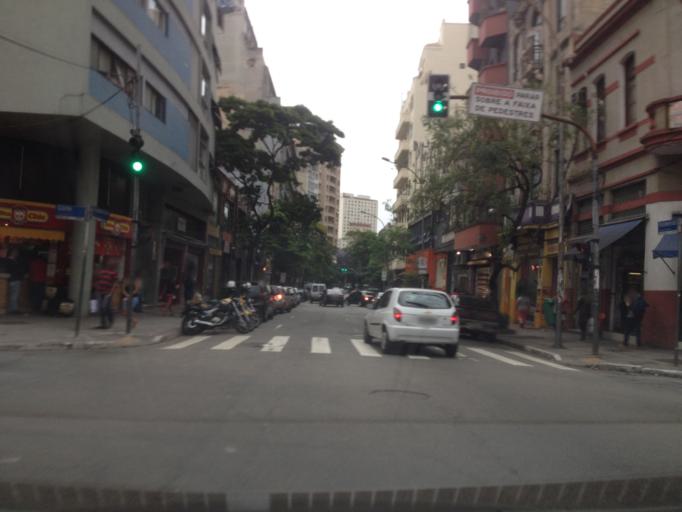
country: BR
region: Sao Paulo
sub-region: Sao Paulo
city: Sao Paulo
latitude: -23.5376
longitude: -46.6509
